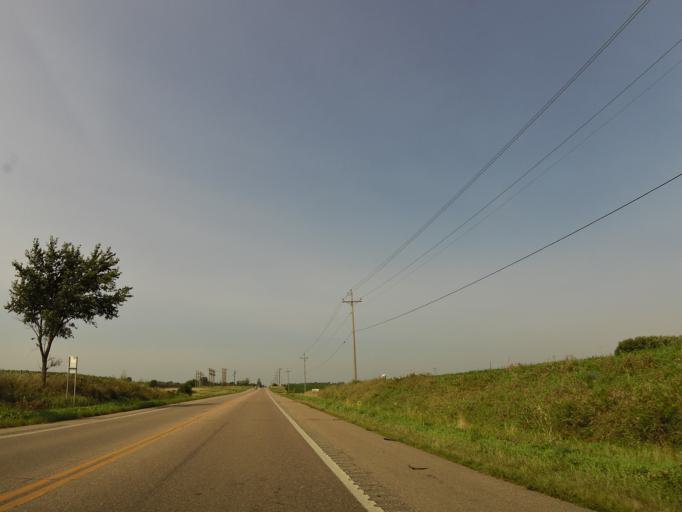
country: US
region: Minnesota
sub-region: Carver County
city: Young America (historical)
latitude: 44.7671
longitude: -93.8538
